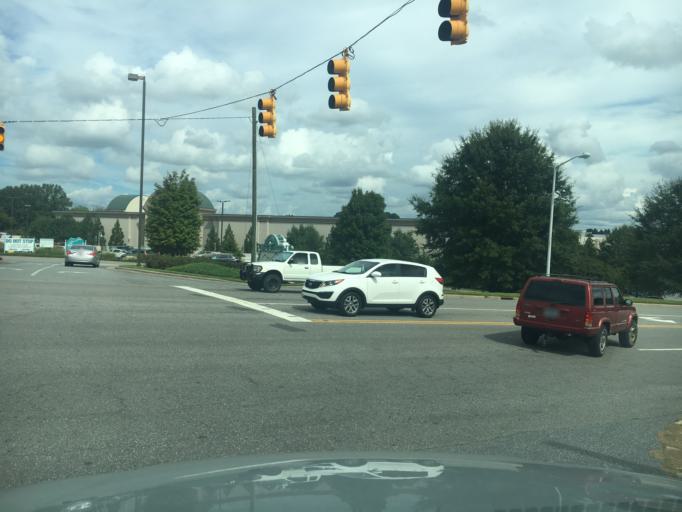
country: US
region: North Carolina
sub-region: Catawba County
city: Hickory
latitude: 35.7022
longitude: -81.3078
